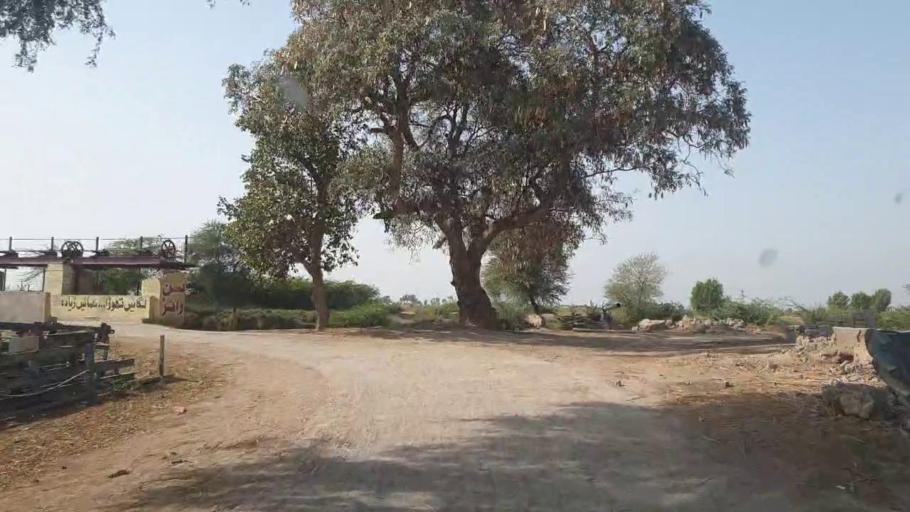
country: PK
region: Sindh
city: Kario
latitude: 24.5766
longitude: 68.4963
